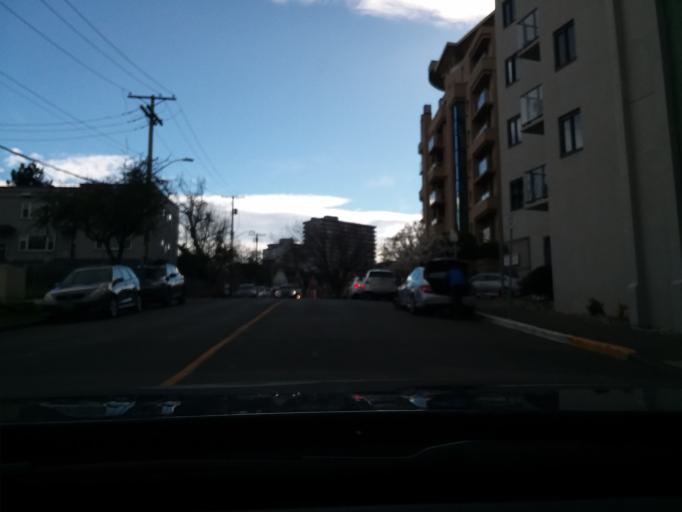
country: CA
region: British Columbia
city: Victoria
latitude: 48.4195
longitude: -123.3650
